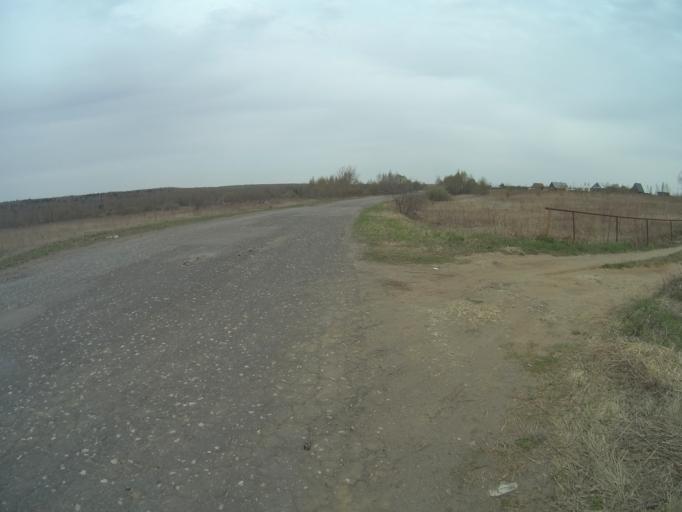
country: RU
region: Vladimir
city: Golovino
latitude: 55.9483
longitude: 40.5937
